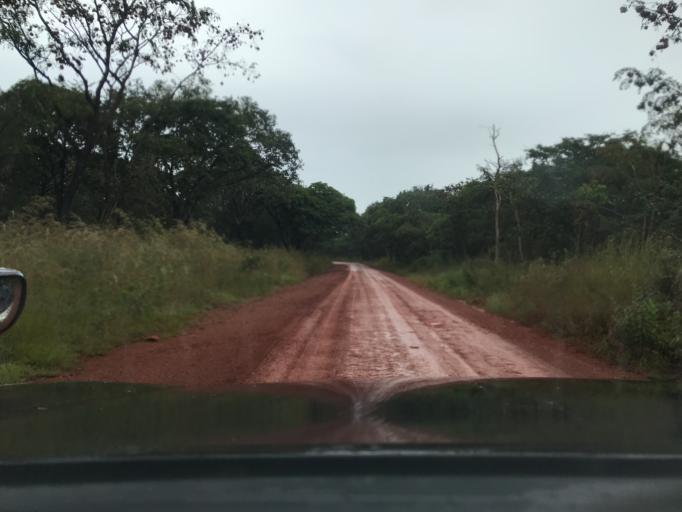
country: TZ
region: Kigoma
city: Uvinza
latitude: -5.2912
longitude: 30.3691
